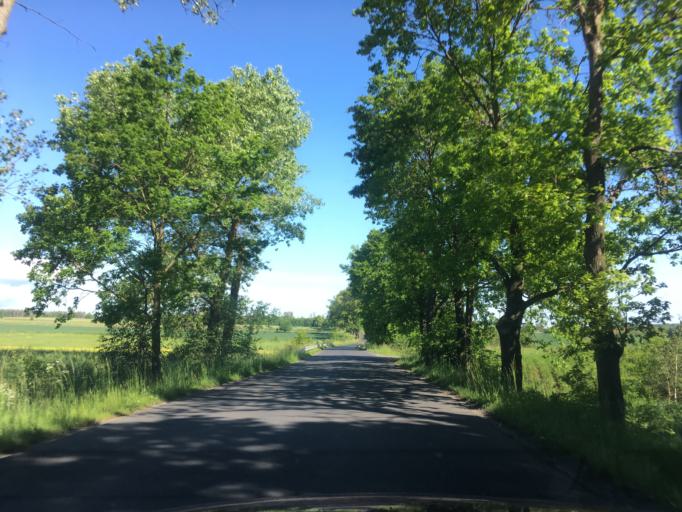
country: PL
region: Lower Silesian Voivodeship
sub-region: Powiat zgorzelecki
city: Sulikow
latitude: 51.0959
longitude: 15.0408
